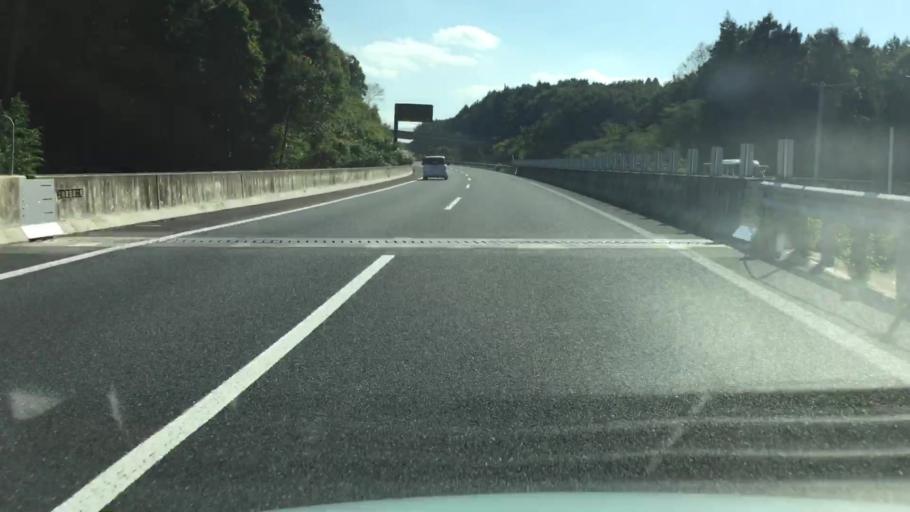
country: JP
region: Ibaraki
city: Tomobe
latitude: 36.3411
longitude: 140.2666
